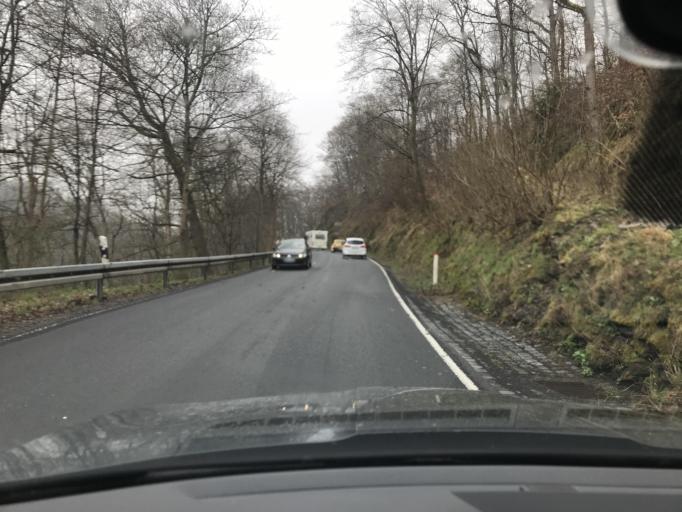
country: DE
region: Saxony-Anhalt
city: Harzgerode
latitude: 51.6669
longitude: 11.1354
